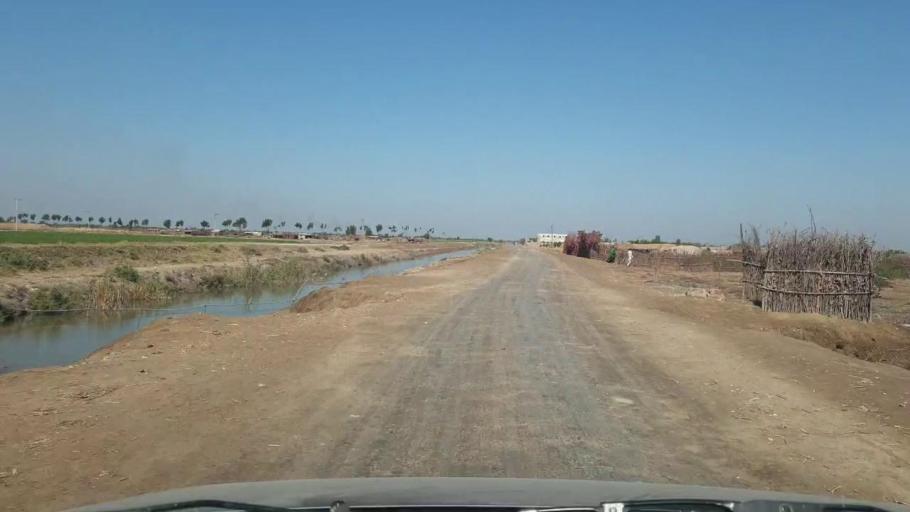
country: PK
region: Sindh
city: Mirwah Gorchani
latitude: 25.3155
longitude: 69.1249
